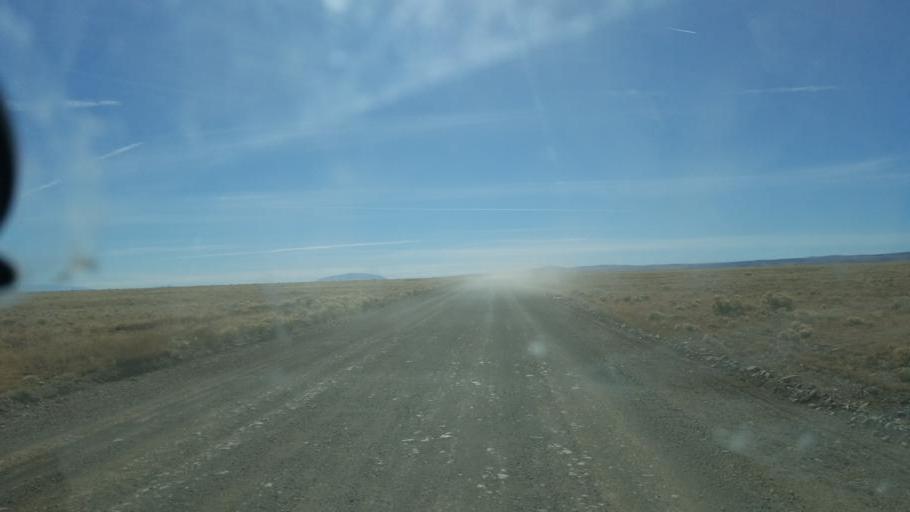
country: US
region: Colorado
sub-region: Rio Grande County
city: Monte Vista
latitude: 37.3475
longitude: -106.1491
